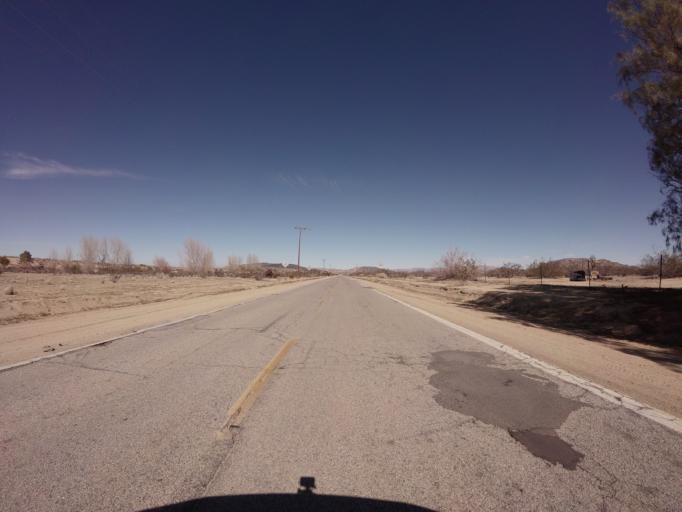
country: US
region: California
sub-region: San Bernardino County
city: Yucca Valley
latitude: 34.2665
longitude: -116.4045
